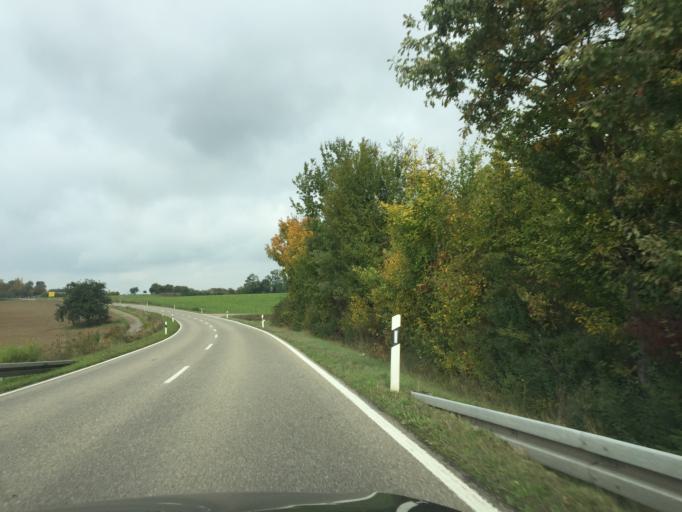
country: DE
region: Baden-Wuerttemberg
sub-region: Karlsruhe Region
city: Bretten
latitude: 49.0964
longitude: 8.7191
